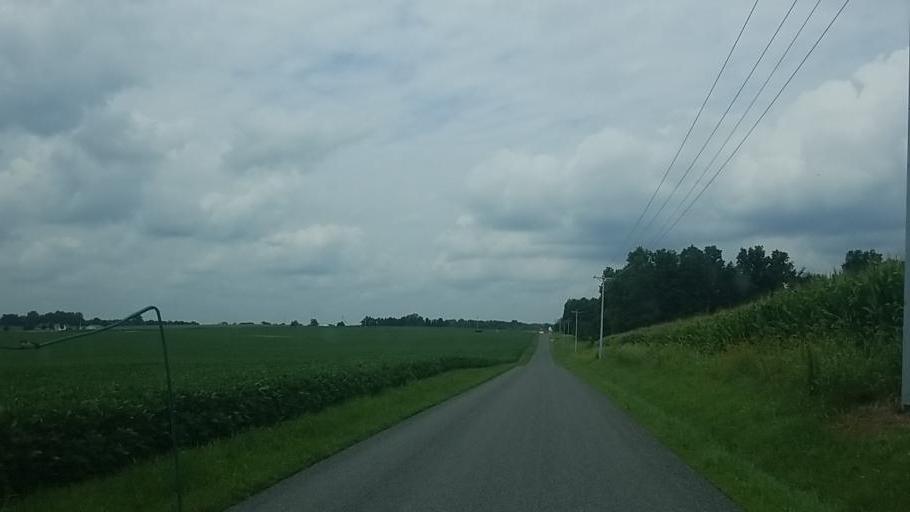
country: US
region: Ohio
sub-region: Licking County
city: Utica
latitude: 40.2368
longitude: -82.3916
